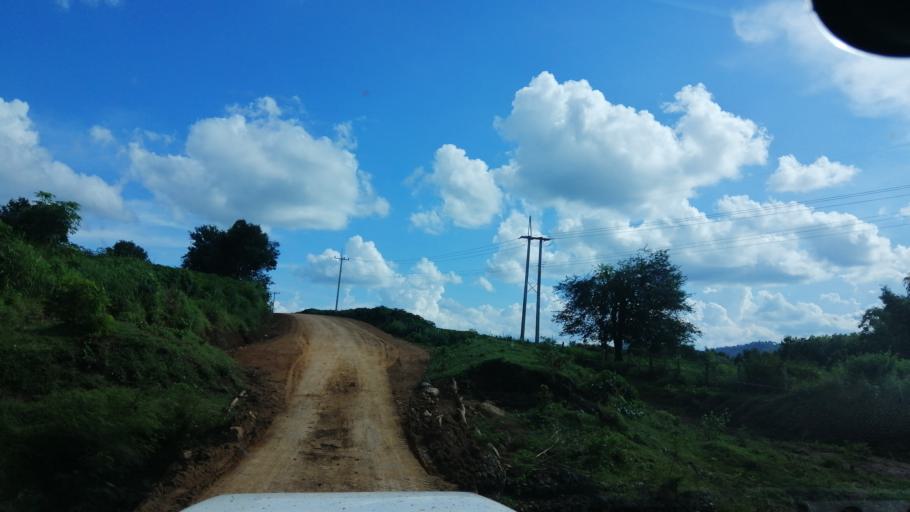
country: TH
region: Uttaradit
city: Ban Khok
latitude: 17.8950
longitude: 101.2172
